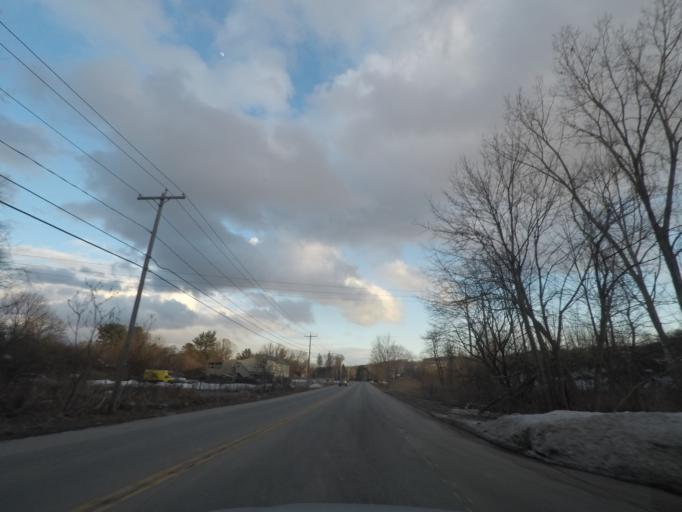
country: US
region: New York
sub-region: Montgomery County
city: Saint Johnsville
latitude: 43.0013
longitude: -74.7025
